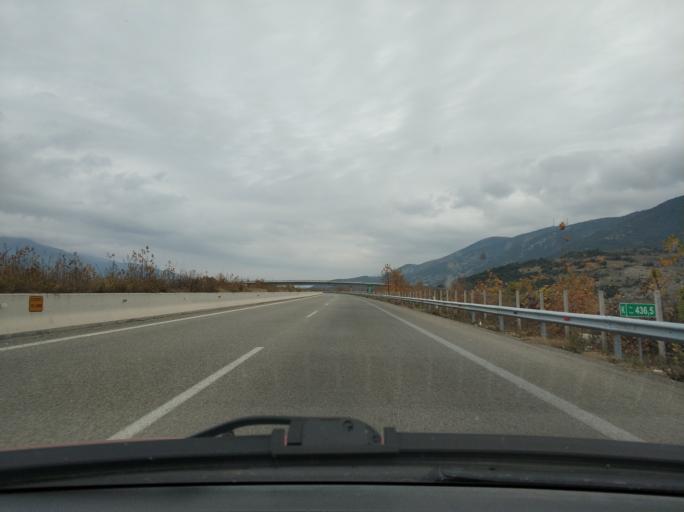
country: GR
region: East Macedonia and Thrace
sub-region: Nomos Kavalas
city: Nikisiani
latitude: 40.8274
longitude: 24.0941
